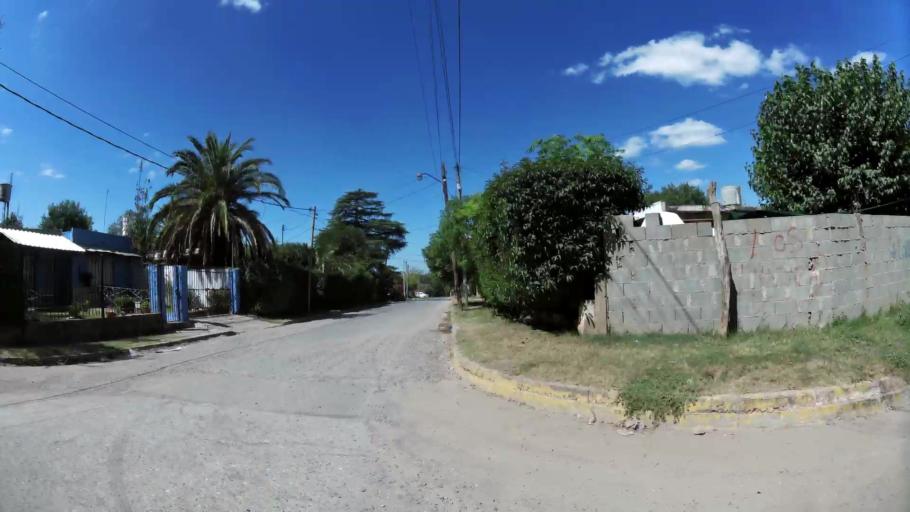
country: AR
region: Cordoba
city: Saldan
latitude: -31.2961
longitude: -64.3047
